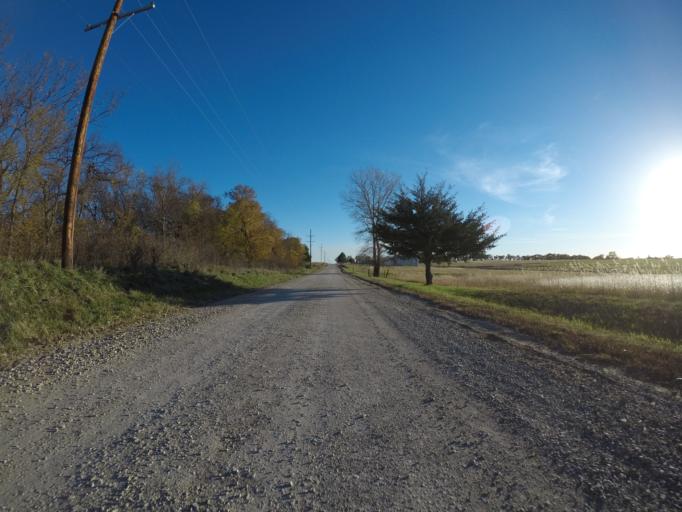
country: US
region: Kansas
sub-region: Riley County
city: Manhattan
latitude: 39.2579
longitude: -96.6819
